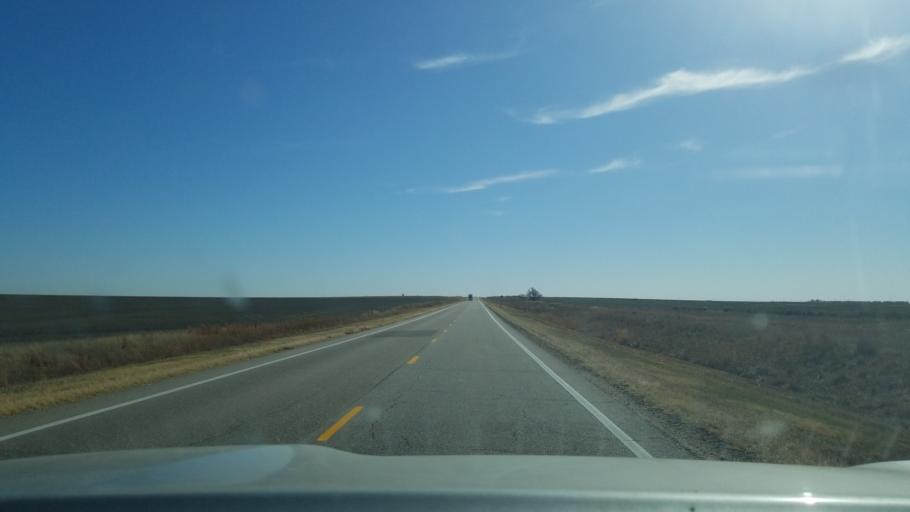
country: US
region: Kansas
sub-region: Ford County
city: Dodge City
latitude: 37.5836
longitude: -99.6799
